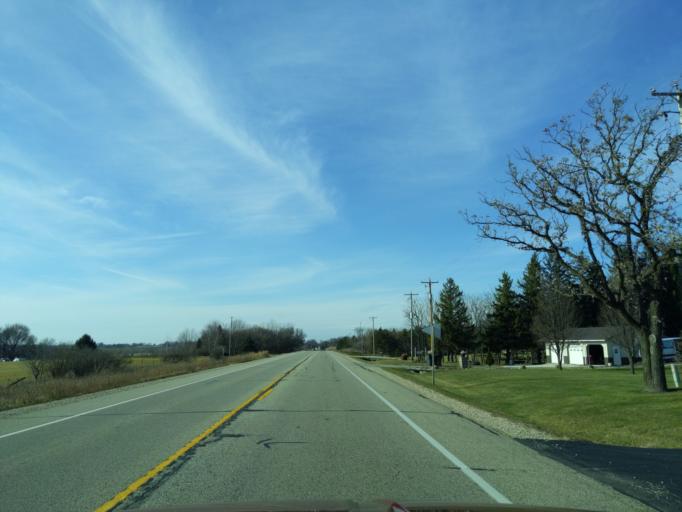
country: US
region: Wisconsin
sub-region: Walworth County
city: Whitewater
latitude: 42.8060
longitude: -88.6603
